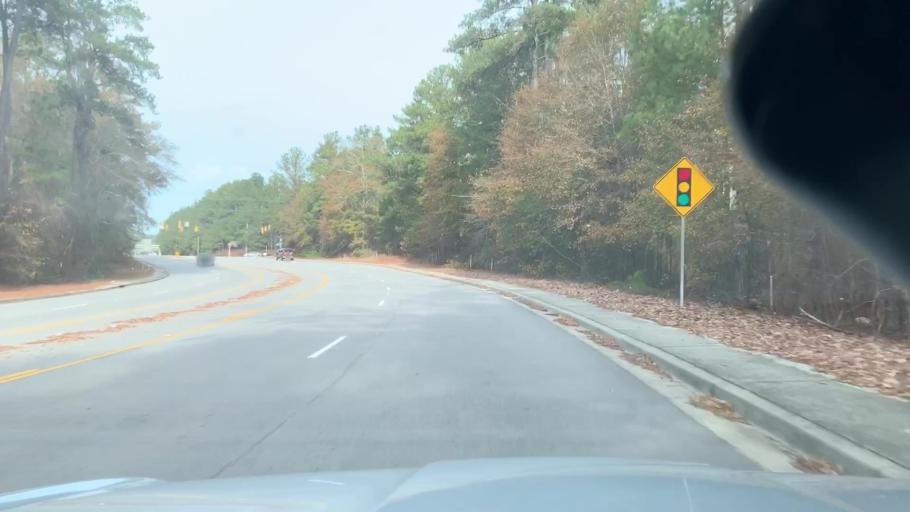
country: US
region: South Carolina
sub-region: Richland County
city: Dentsville
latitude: 34.0675
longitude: -80.9472
